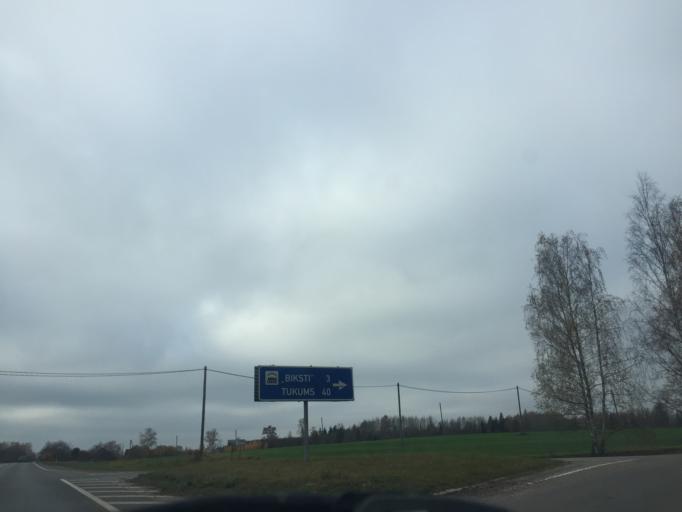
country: LV
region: Jaunpils
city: Jaunpils
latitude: 56.6632
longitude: 22.9628
